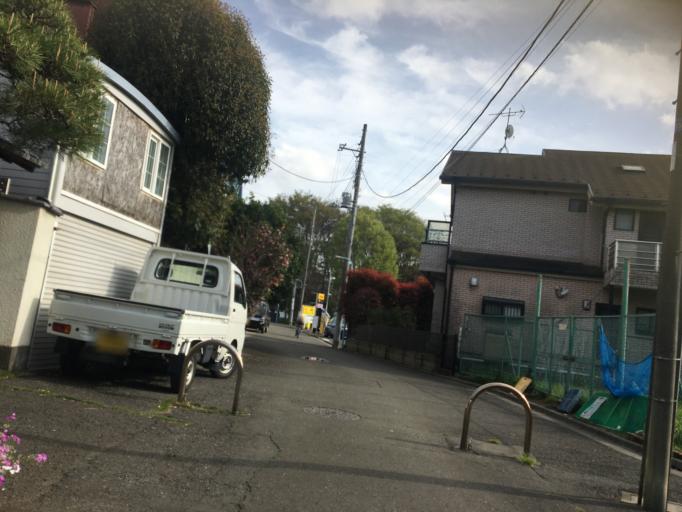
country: JP
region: Tokyo
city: Tokyo
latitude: 35.6932
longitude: 139.6254
